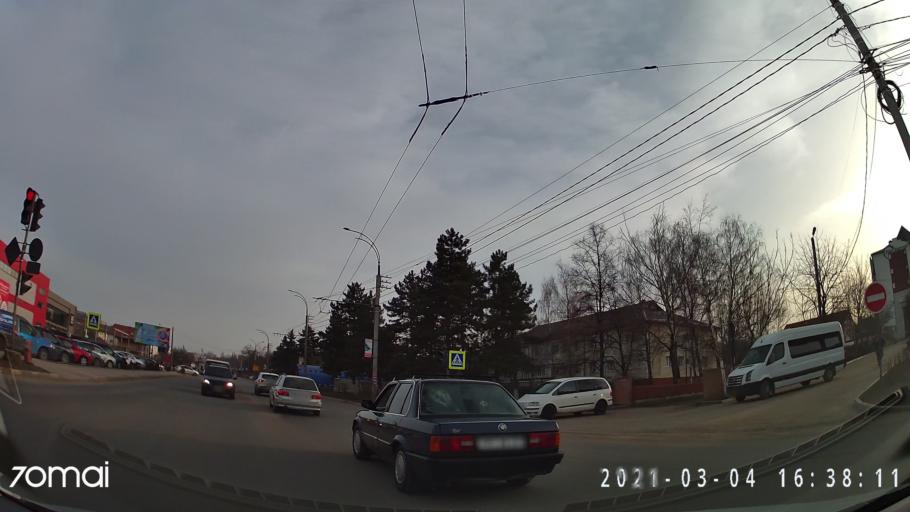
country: MD
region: Balti
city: Balti
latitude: 47.7819
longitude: 27.8902
